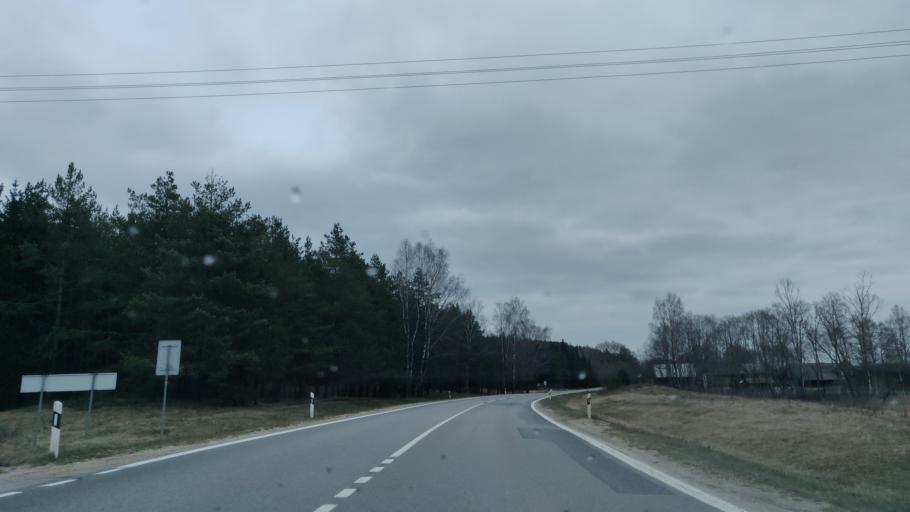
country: LT
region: Vilnius County
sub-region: Trakai
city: Rudiskes
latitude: 54.5966
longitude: 24.7616
